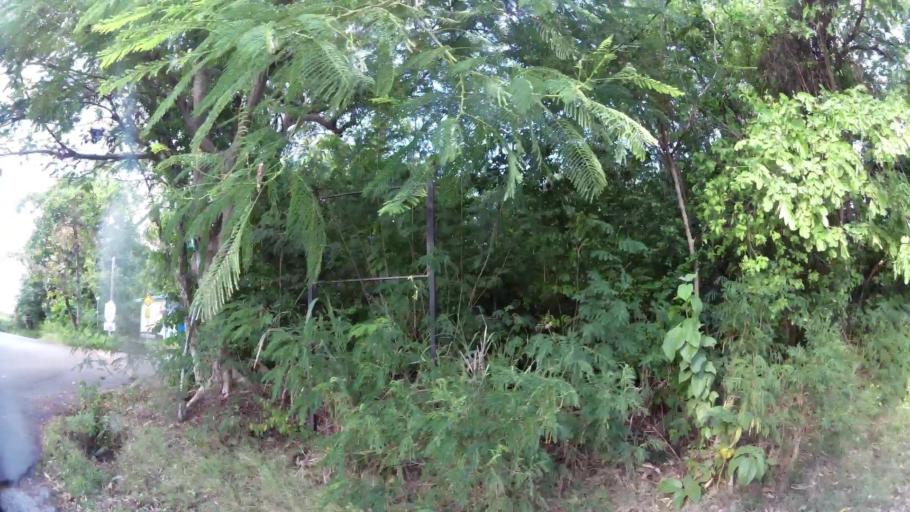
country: LC
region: Gros-Islet
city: Gros Islet
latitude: 14.1000
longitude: -60.9437
